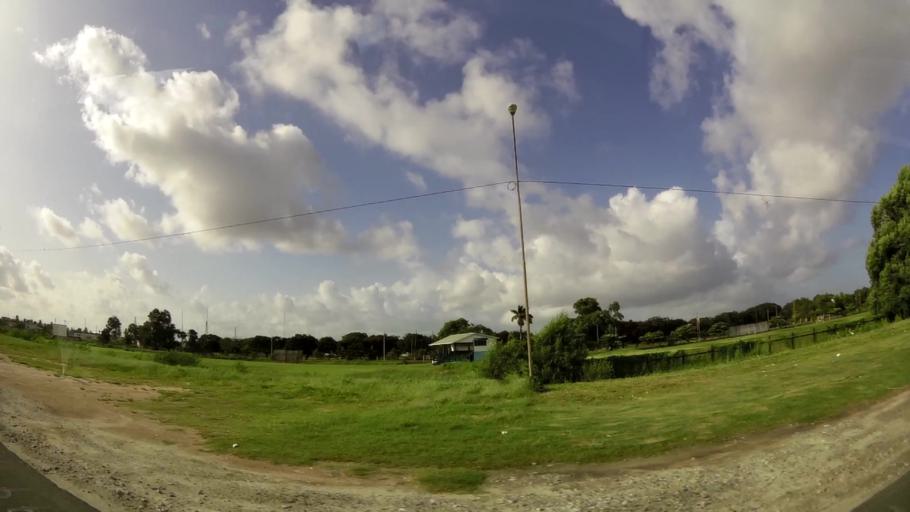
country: GY
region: Demerara-Mahaica
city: Georgetown
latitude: 6.8250
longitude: -58.1500
